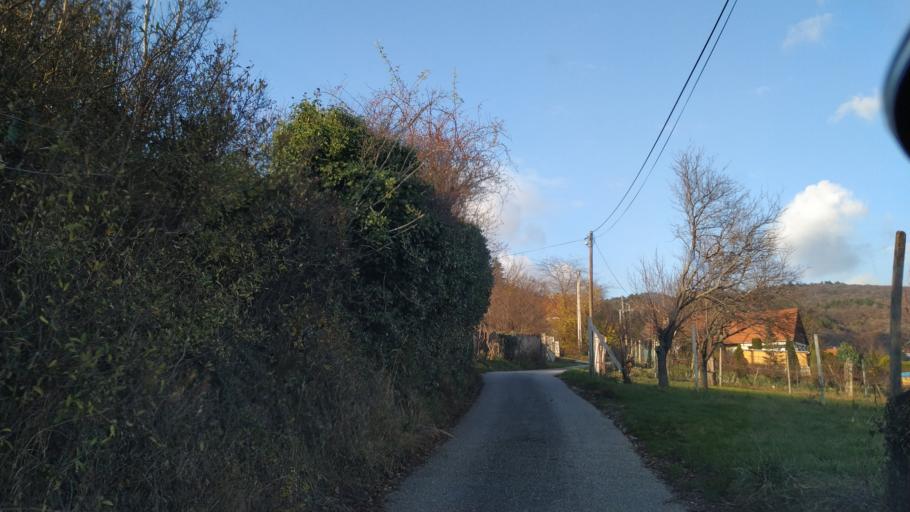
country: HU
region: Zala
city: Vonyarcvashegy
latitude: 46.7817
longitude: 17.3627
